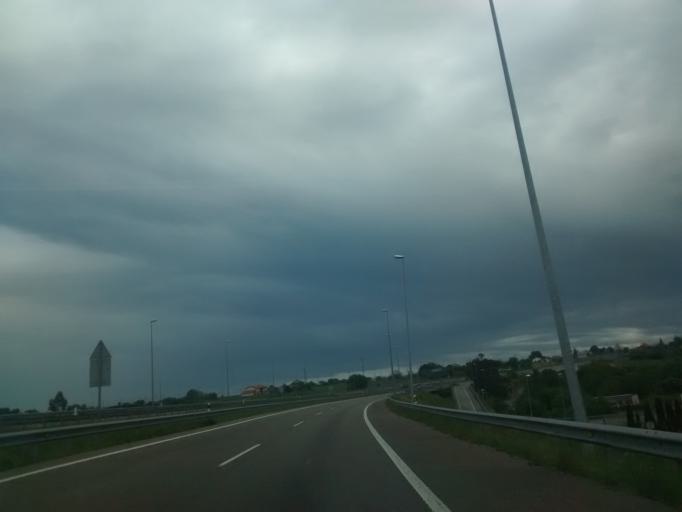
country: ES
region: Asturias
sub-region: Province of Asturias
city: Arriba
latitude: 43.5122
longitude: -5.5726
